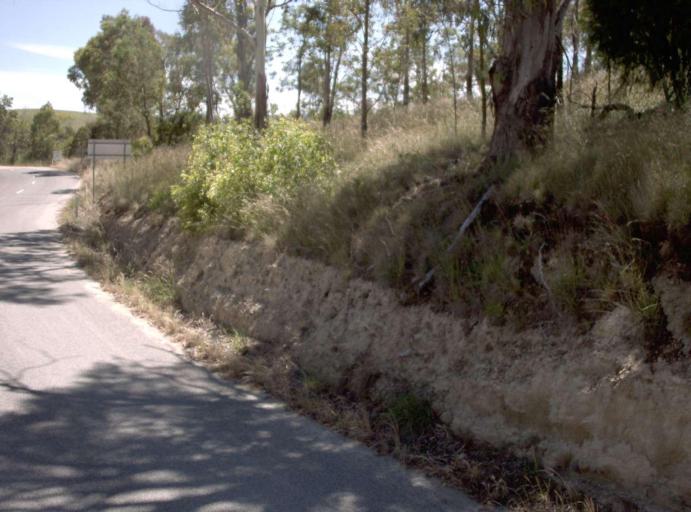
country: AU
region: Victoria
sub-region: East Gippsland
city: Lakes Entrance
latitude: -37.4529
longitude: 148.1917
